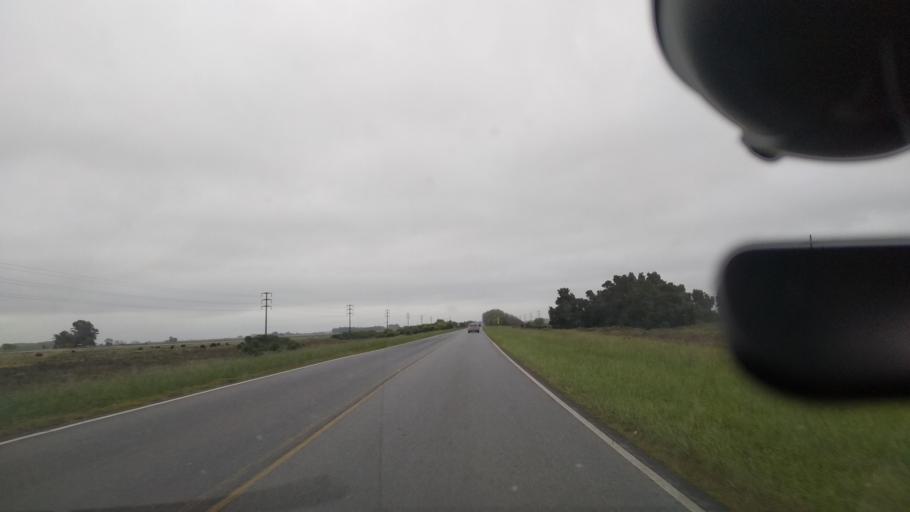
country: AR
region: Buenos Aires
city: Veronica
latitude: -35.3688
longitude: -57.3890
